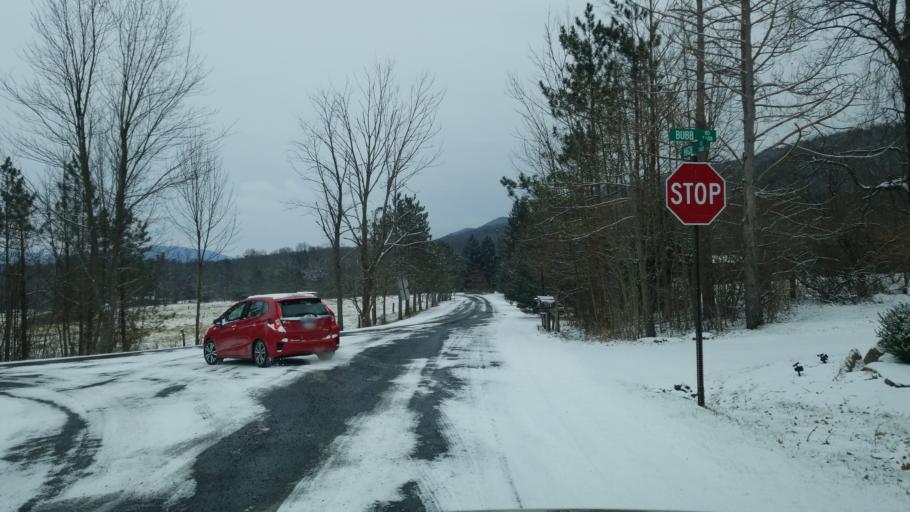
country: US
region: Pennsylvania
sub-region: Centre County
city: Centre Hall
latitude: 40.7747
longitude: -77.6700
